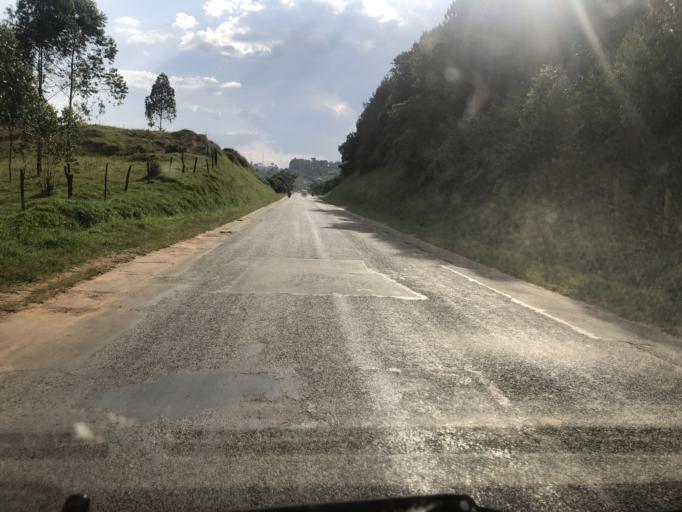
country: UG
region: Western Region
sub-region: Bushenyi District
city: Bushenyi
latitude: -0.5435
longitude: 30.2138
